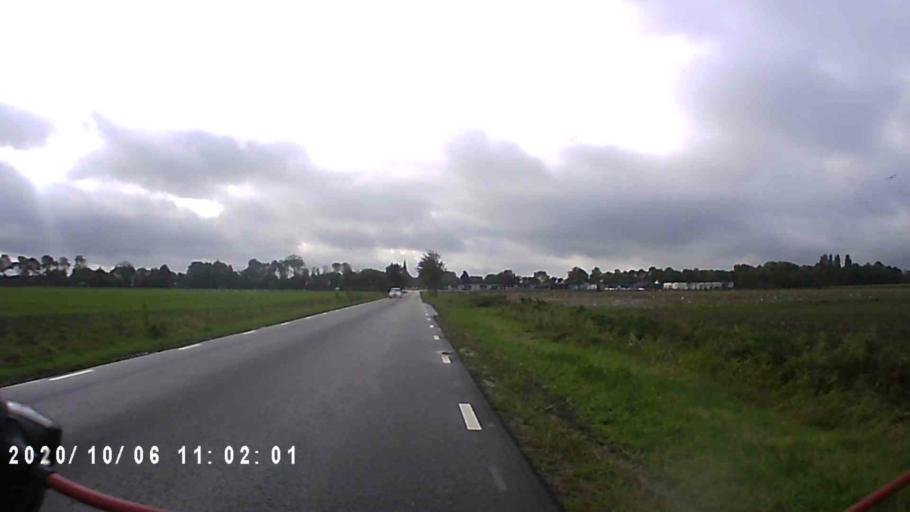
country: NL
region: Groningen
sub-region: Gemeente De Marne
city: Ulrum
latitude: 53.3657
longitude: 6.3735
